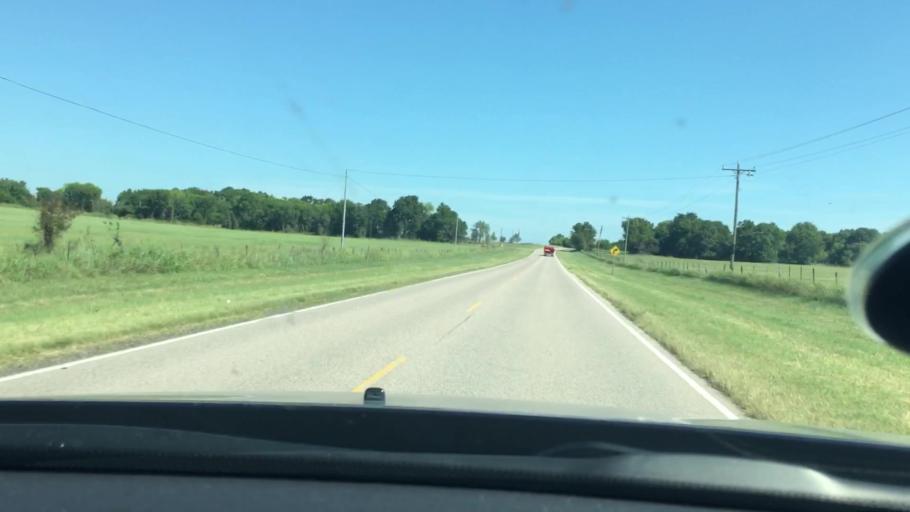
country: US
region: Oklahoma
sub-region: Johnston County
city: Tishomingo
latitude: 34.4673
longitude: -96.6362
